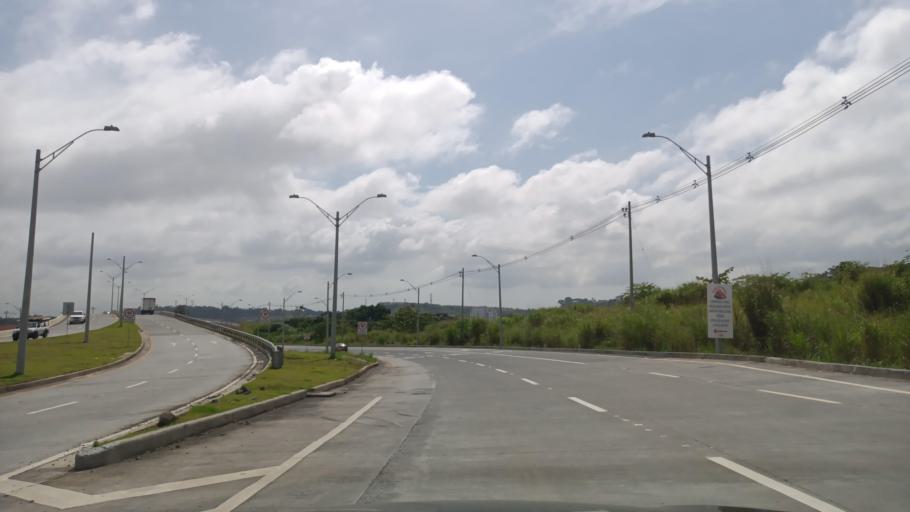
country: PA
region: Panama
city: San Miguelito
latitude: 9.0917
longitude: -79.4644
